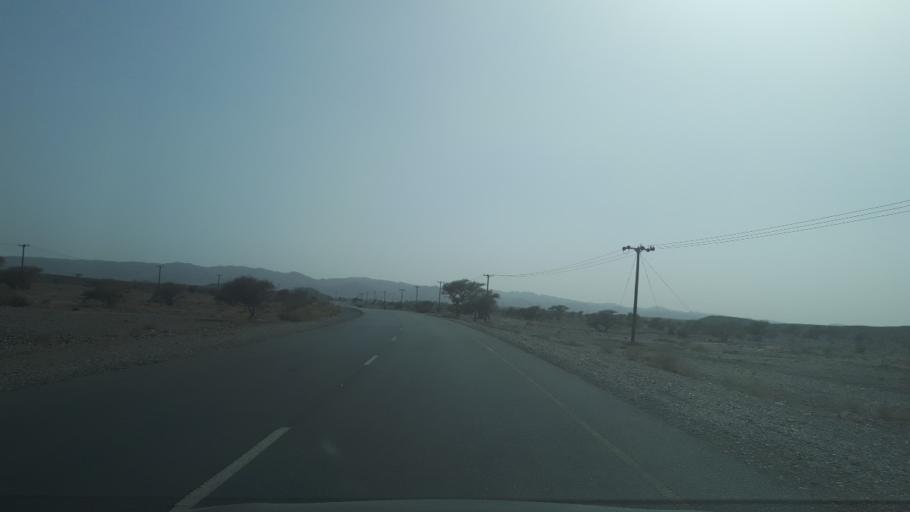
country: OM
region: Az Zahirah
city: `Ibri
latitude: 23.0963
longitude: 56.8465
